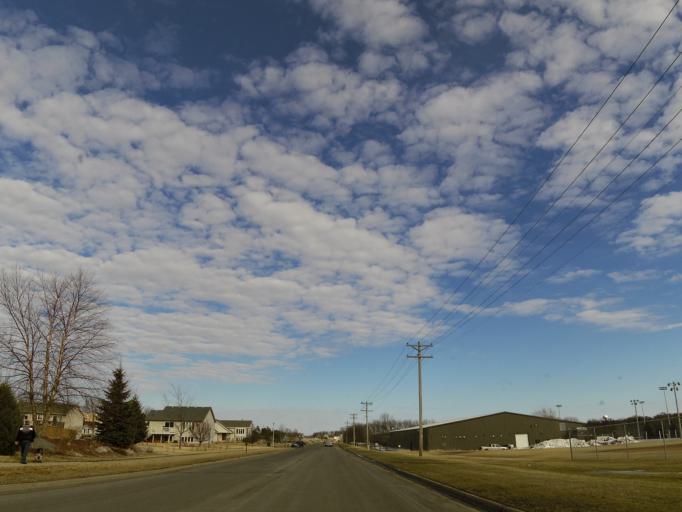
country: US
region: Minnesota
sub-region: Le Sueur County
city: New Prague
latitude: 44.5579
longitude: -93.5808
